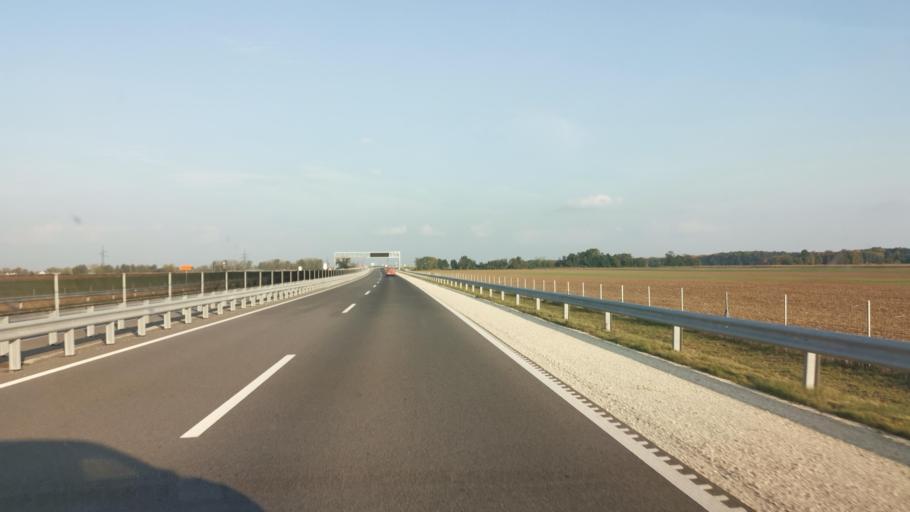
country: HU
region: Gyor-Moson-Sopron
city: Kapuvar
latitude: 47.5701
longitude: 17.0245
